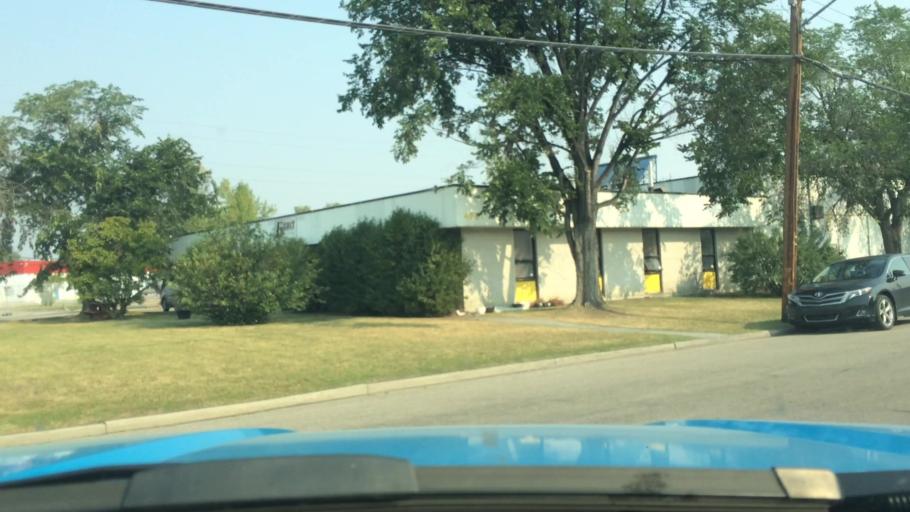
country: CA
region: Alberta
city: Calgary
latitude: 51.0118
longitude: -114.0567
